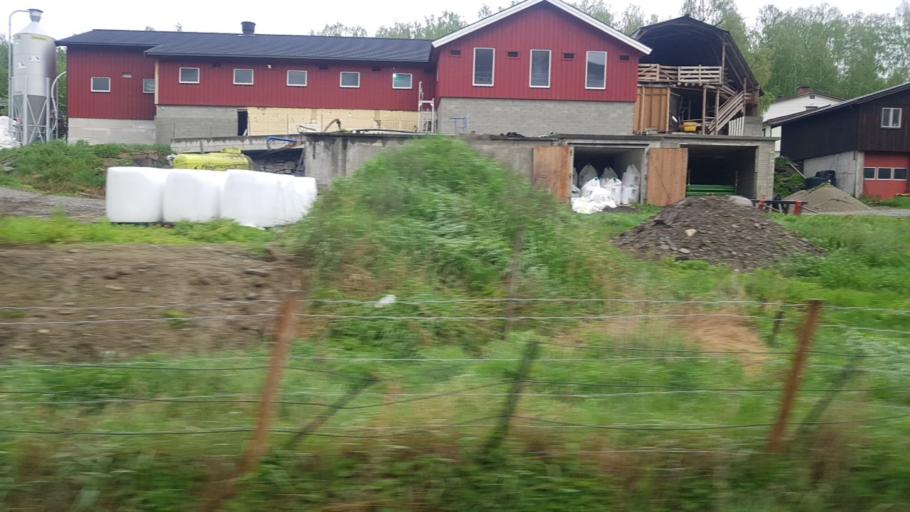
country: NO
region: Oppland
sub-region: Sor-Fron
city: Hundorp
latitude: 61.5662
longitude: 9.9236
